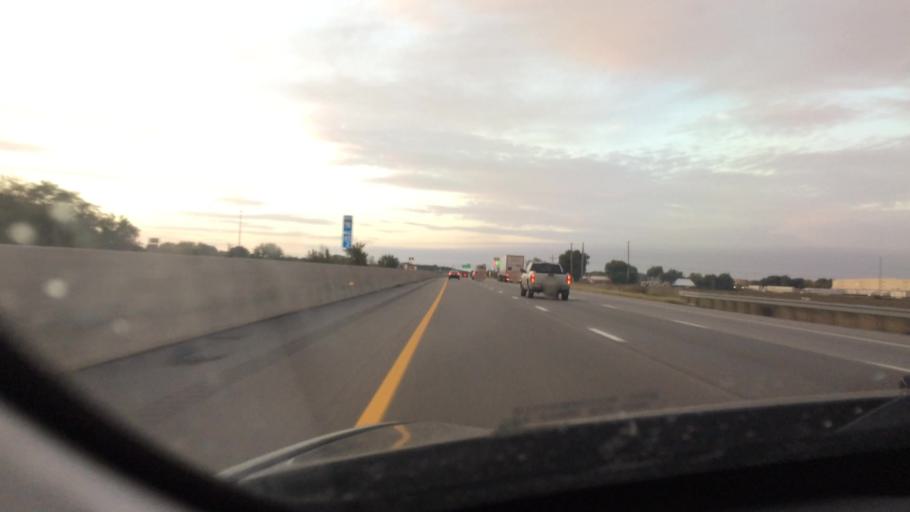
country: US
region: Ohio
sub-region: Wood County
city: North Baltimore
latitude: 41.1462
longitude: -83.6589
